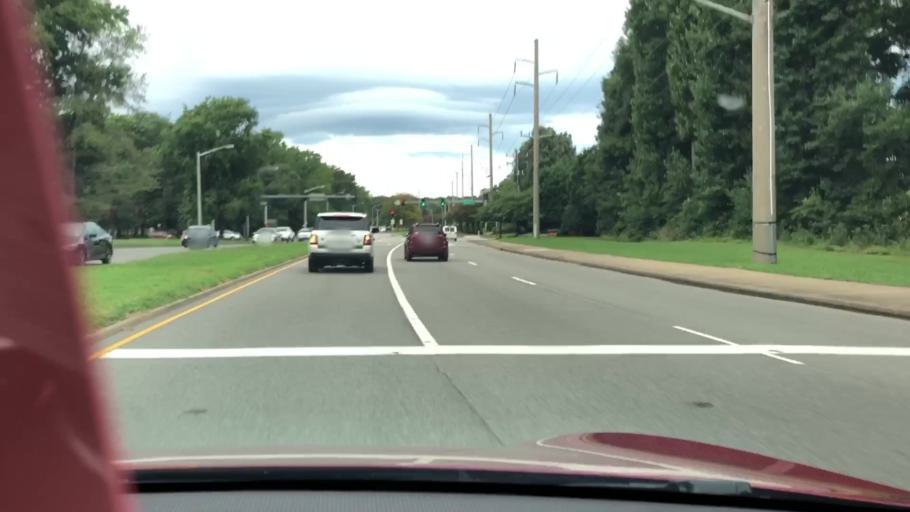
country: US
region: Virginia
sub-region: City of Virginia Beach
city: Virginia Beach
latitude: 36.8852
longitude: -76.0481
